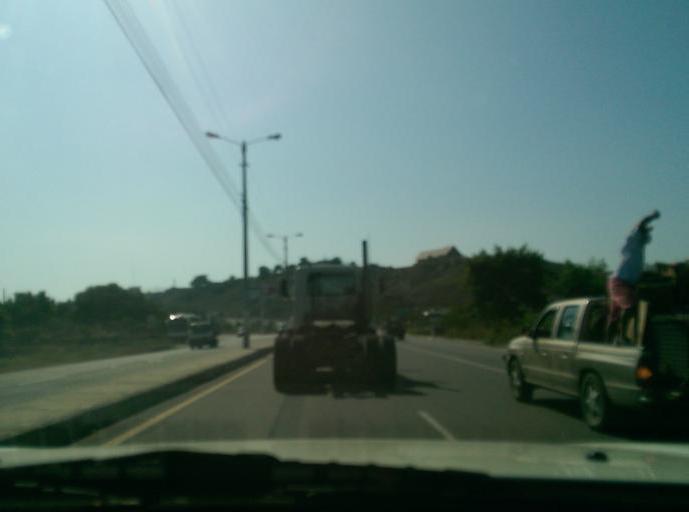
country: EC
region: Manabi
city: Manta
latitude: -0.9621
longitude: -80.7377
